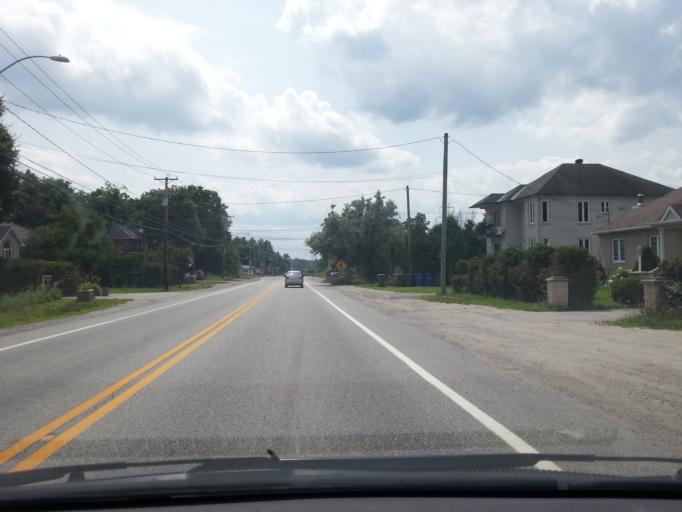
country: CA
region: Quebec
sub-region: Outaouais
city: Gatineau
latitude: 45.5074
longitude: -75.7629
